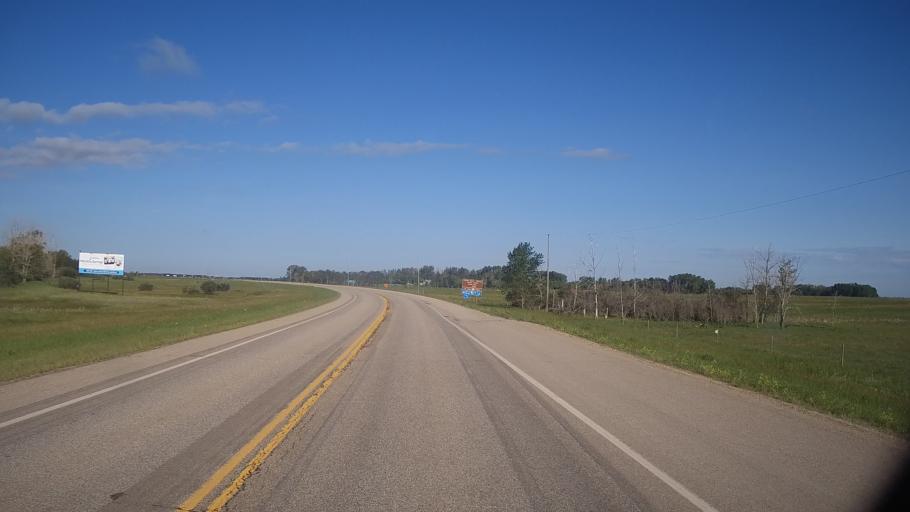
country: CA
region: Saskatchewan
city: Lanigan
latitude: 51.8744
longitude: -105.1831
